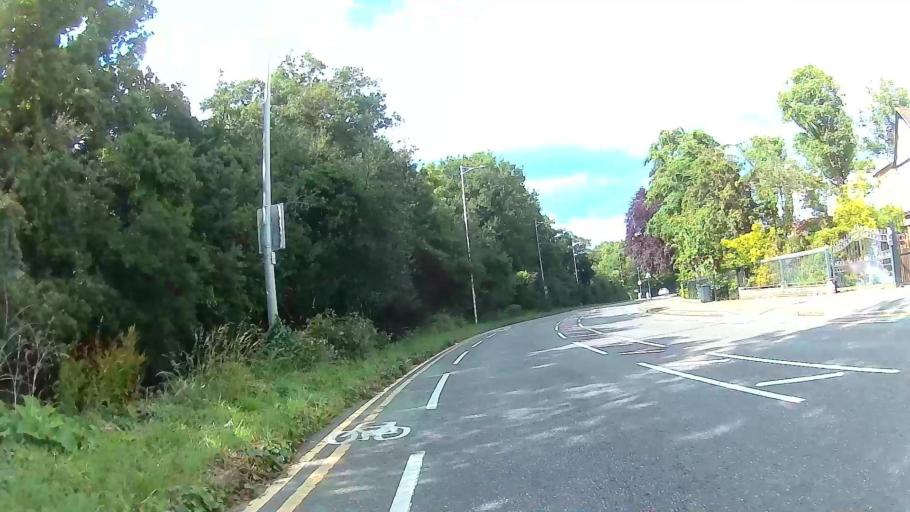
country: GB
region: England
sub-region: Greater London
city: Woodford Green
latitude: 51.5791
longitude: 0.0177
